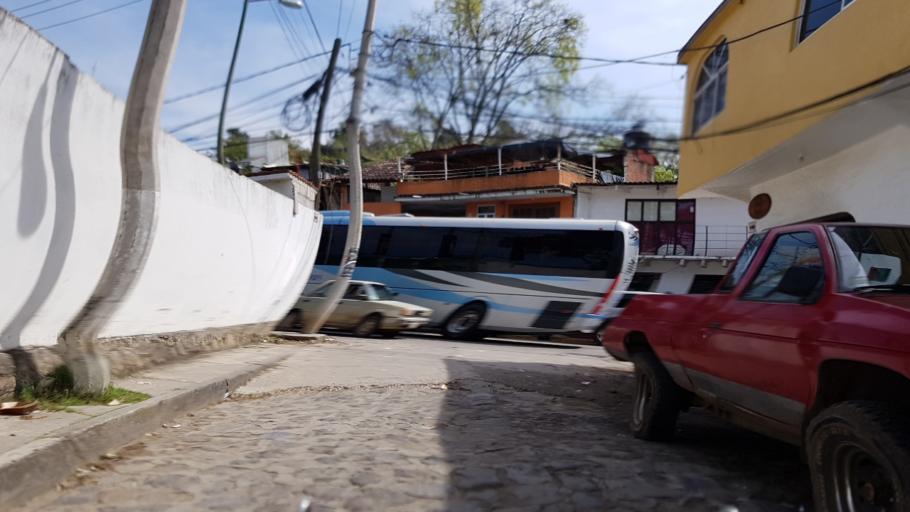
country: MX
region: Mexico
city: Valle de Bravo
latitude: 19.2027
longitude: -100.1360
